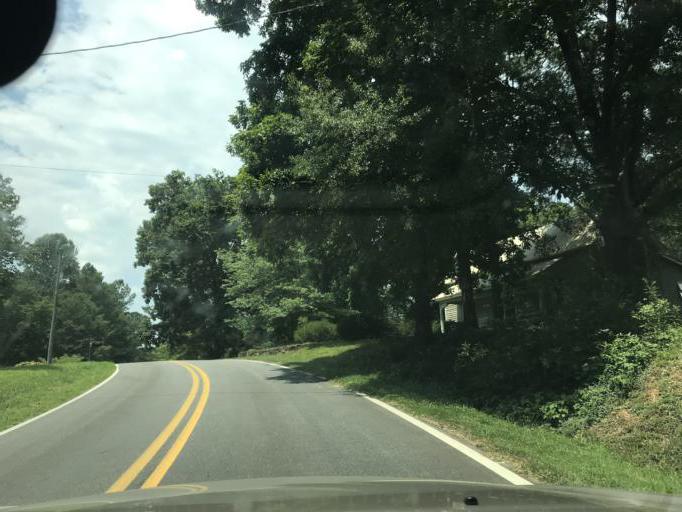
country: US
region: Georgia
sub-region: Dawson County
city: Dawsonville
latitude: 34.3342
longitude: -84.1875
